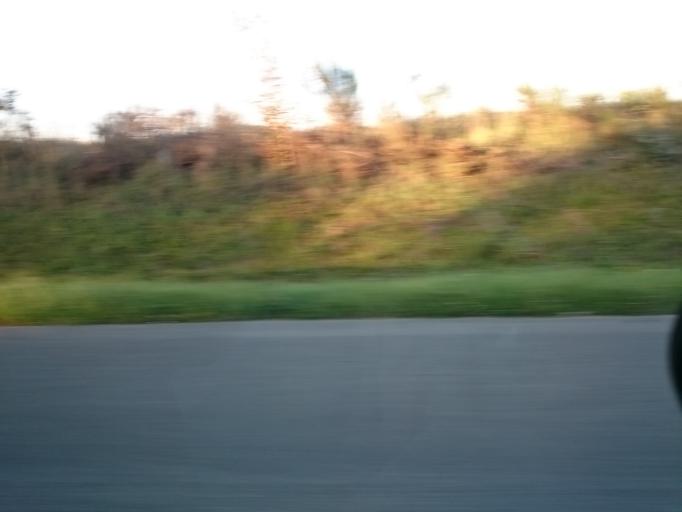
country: FR
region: Brittany
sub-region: Departement du Finistere
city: Plouigneau
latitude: 48.5815
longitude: -3.7495
